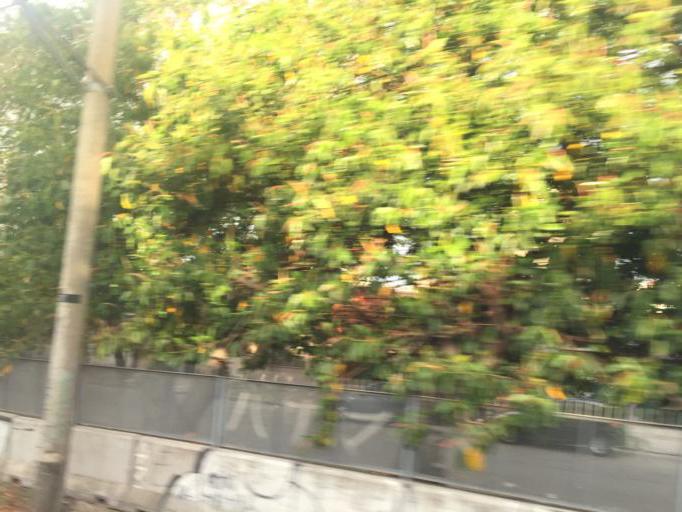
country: AR
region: Buenos Aires
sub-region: Partido de Lanus
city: Lanus
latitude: -34.7024
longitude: -58.3887
